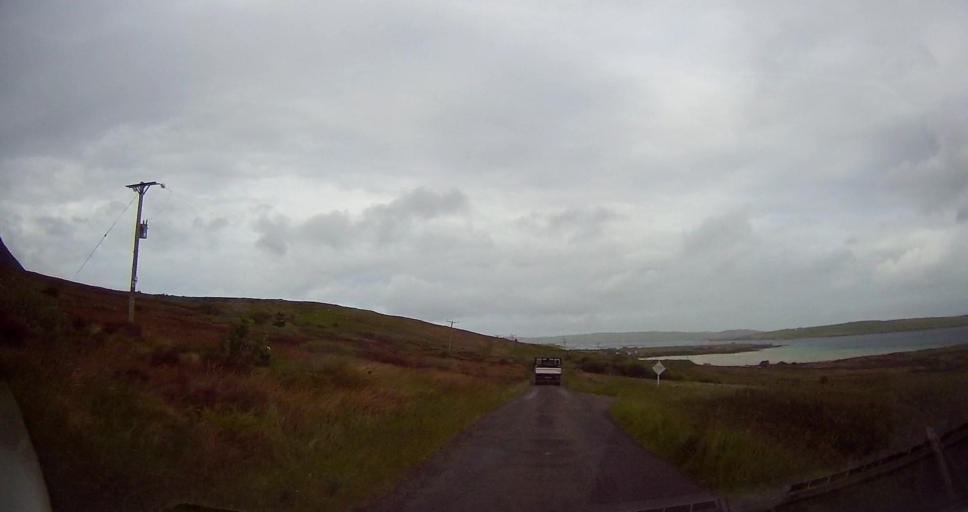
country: GB
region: Scotland
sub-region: Orkney Islands
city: Stromness
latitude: 58.9017
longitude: -3.3160
